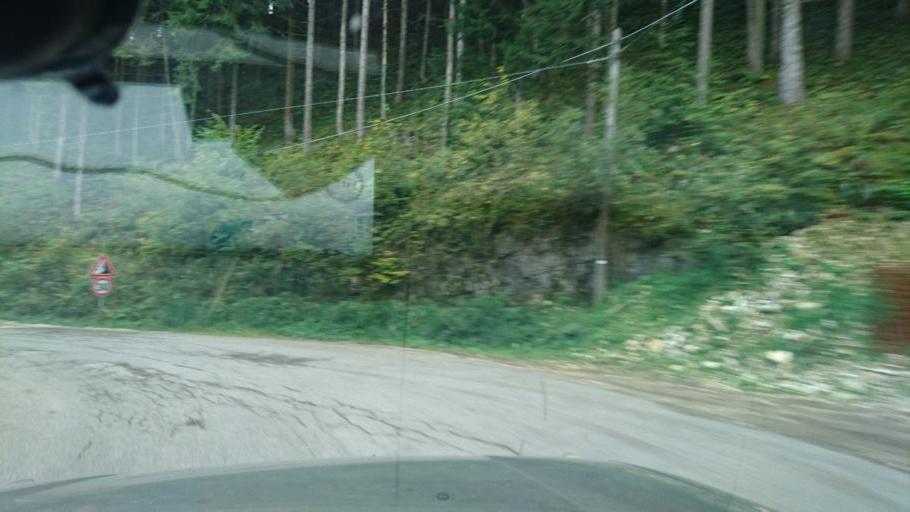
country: IT
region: Veneto
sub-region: Provincia di Vicenza
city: Enego
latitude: 45.9384
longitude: 11.6772
